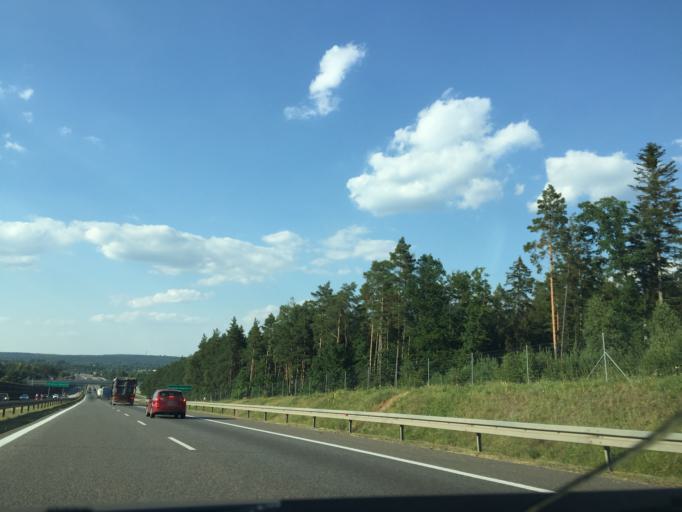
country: PL
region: Swietokrzyskie
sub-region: Powiat skarzyski
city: Suchedniow
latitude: 51.0831
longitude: 20.8364
